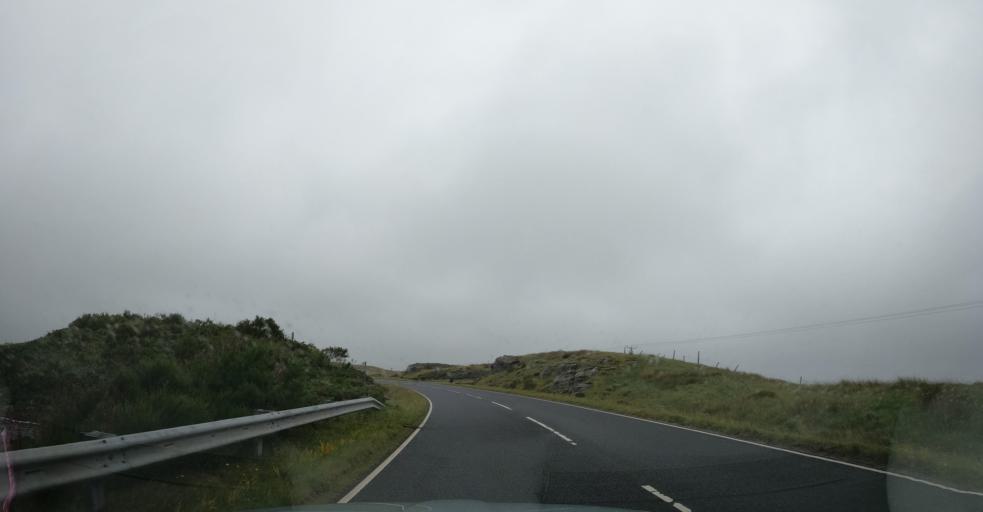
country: GB
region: Scotland
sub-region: Eilean Siar
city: Isle of North Uist
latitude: 57.5999
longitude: -7.1784
